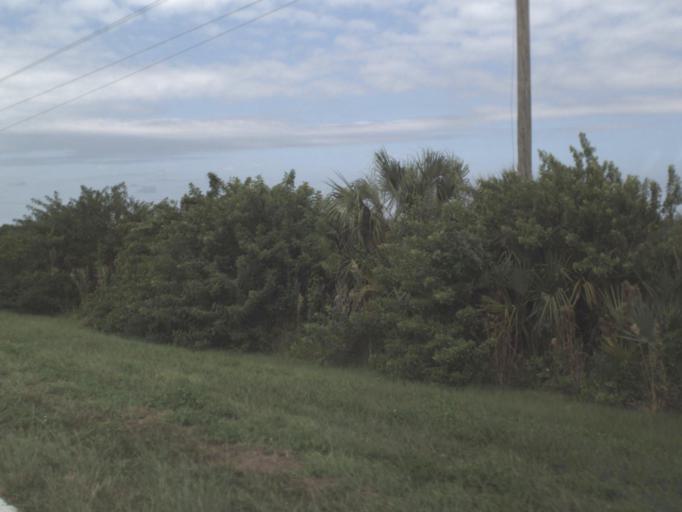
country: US
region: Florida
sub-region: Glades County
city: Moore Haven
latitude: 26.7684
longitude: -81.2092
